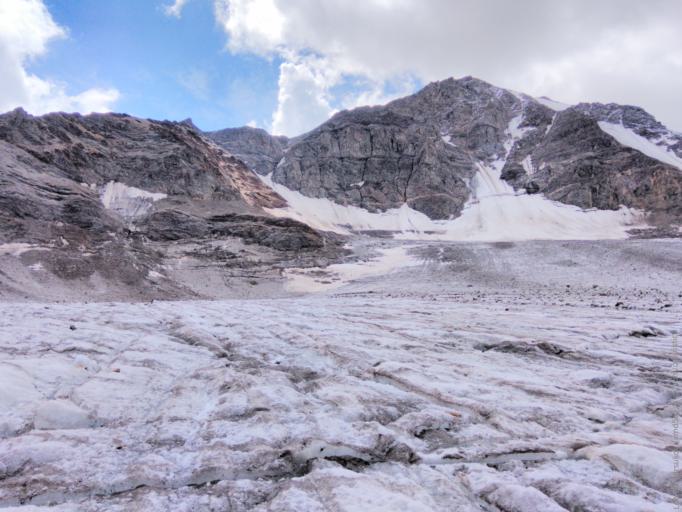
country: RU
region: Kabardino-Balkariya
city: Terskol
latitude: 43.3555
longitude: 42.5558
